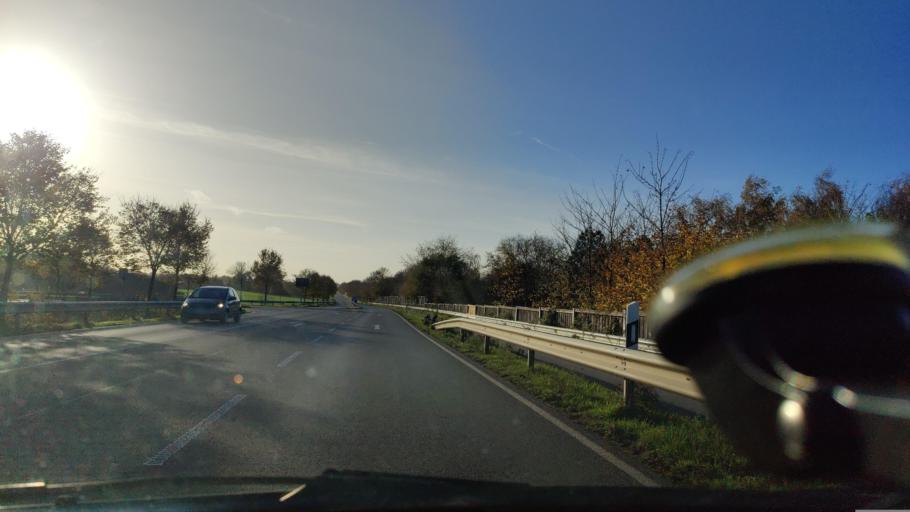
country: DE
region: North Rhine-Westphalia
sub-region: Regierungsbezirk Dusseldorf
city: Kevelaer
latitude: 51.5735
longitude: 6.2584
